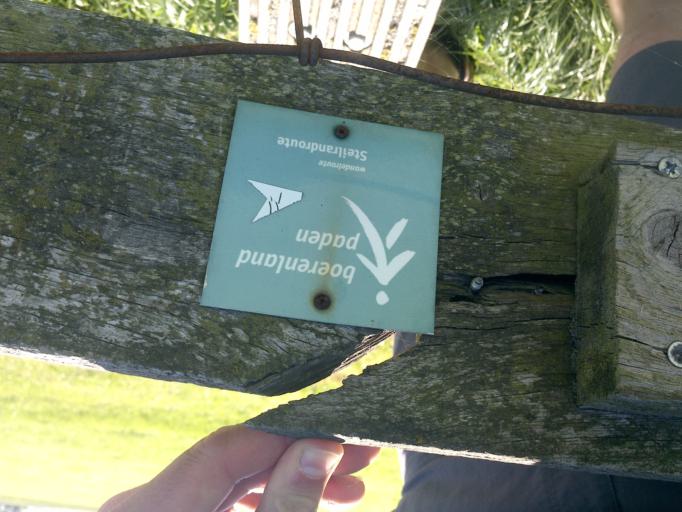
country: NL
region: South Holland
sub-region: Gemeente Rijnwoude
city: Benthuizen
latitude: 52.1092
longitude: 4.5753
